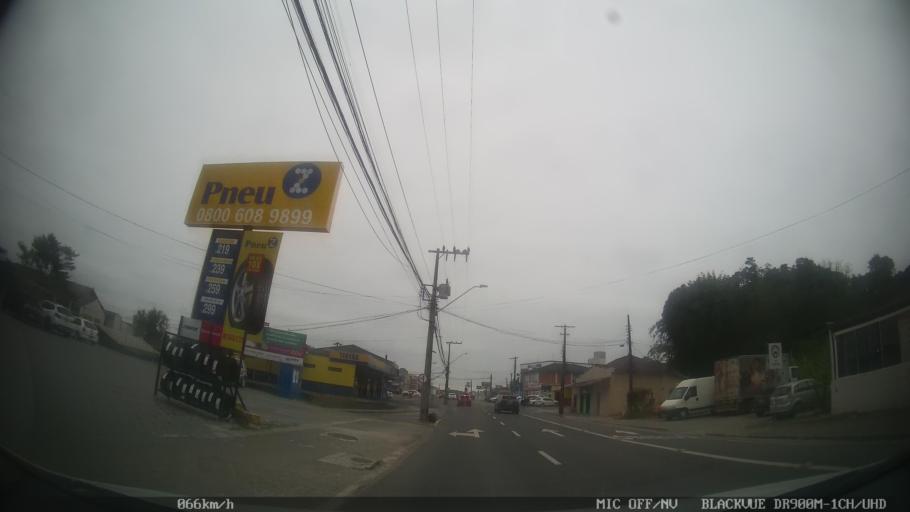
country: BR
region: Santa Catarina
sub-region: Joinville
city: Joinville
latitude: -26.3268
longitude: -48.8454
